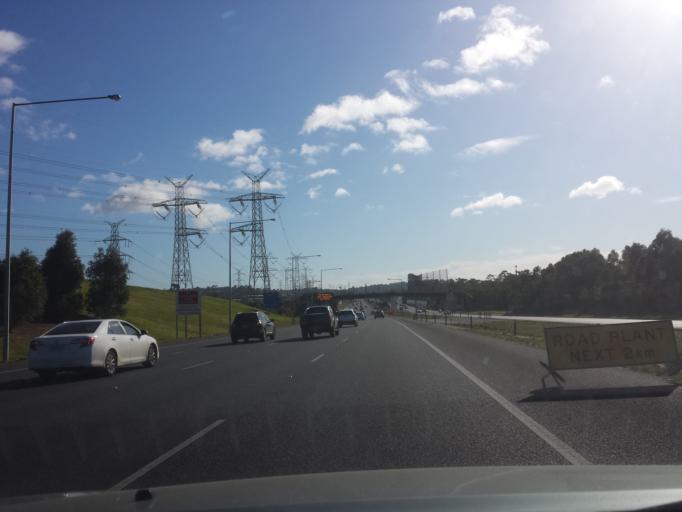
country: AU
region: Victoria
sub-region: Knox
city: Wantirna
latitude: -37.8415
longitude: 145.2176
